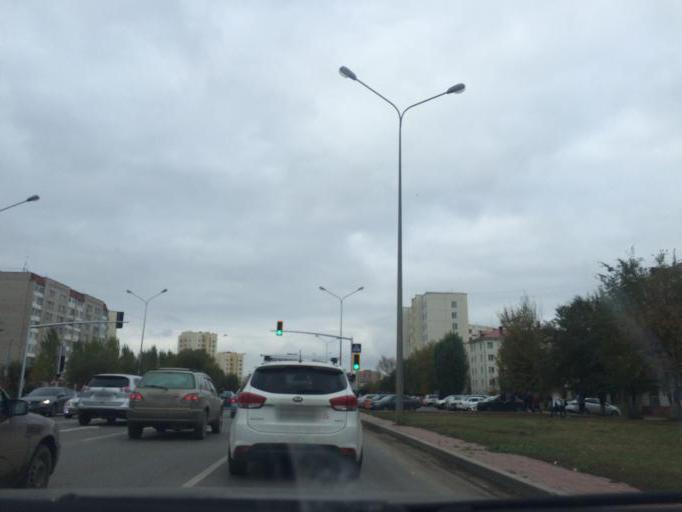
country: KZ
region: Astana Qalasy
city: Astana
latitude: 51.1545
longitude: 71.4792
